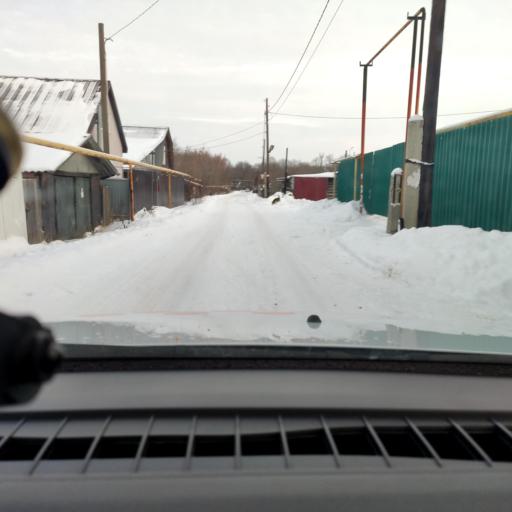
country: RU
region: Samara
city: Novokuybyshevsk
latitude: 53.0904
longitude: 50.0594
